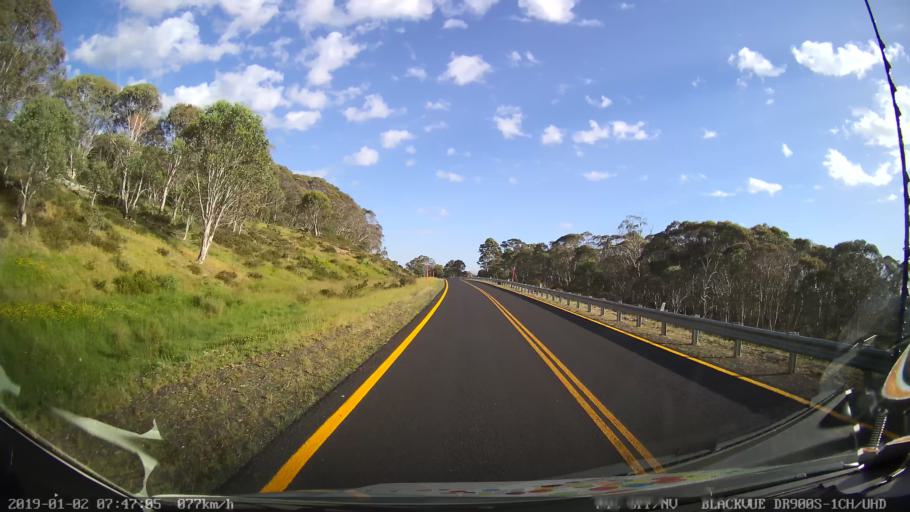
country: AU
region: New South Wales
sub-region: Tumut Shire
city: Tumut
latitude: -35.7685
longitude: 148.5216
